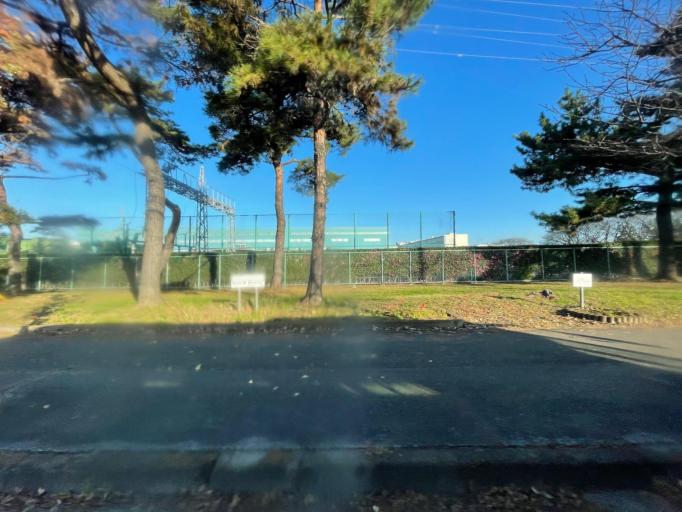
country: JP
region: Ibaraki
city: Koga
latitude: 36.1941
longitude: 139.7581
